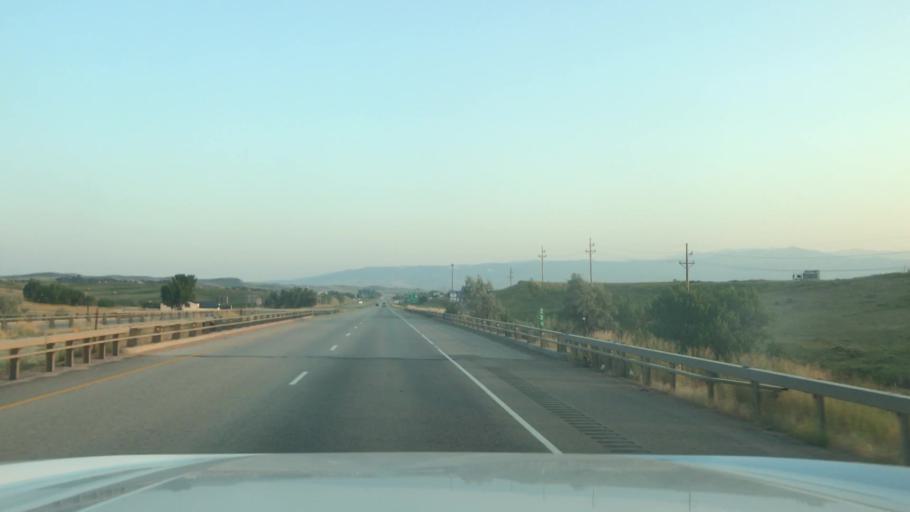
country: US
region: Wyoming
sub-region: Sheridan County
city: Sheridan
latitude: 44.7968
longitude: -106.9369
